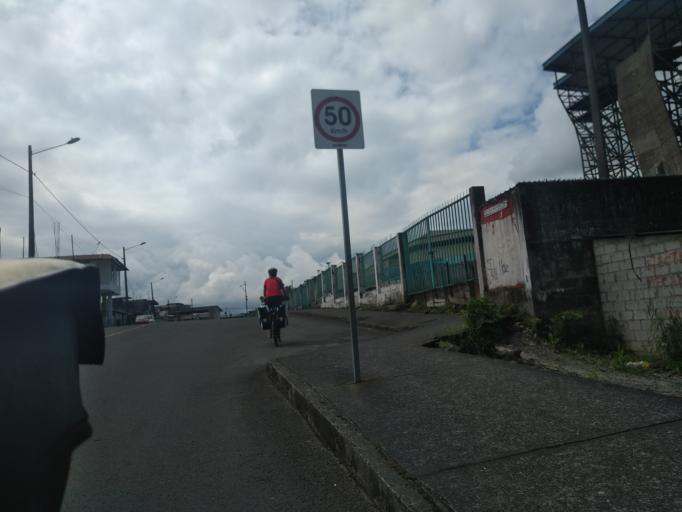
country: EC
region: Pastaza
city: Puyo
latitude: -1.4881
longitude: -78.0030
